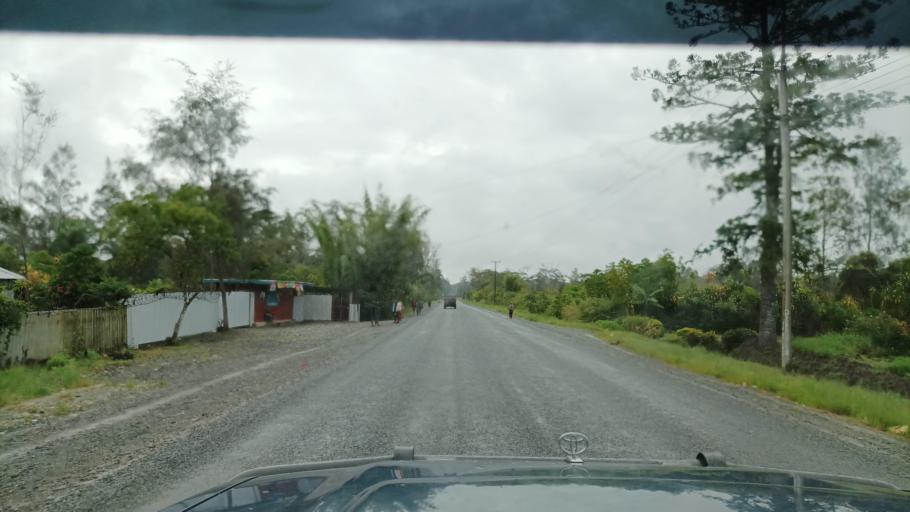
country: PG
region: Western Highlands
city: Rauna
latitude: -5.8240
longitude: 144.3899
